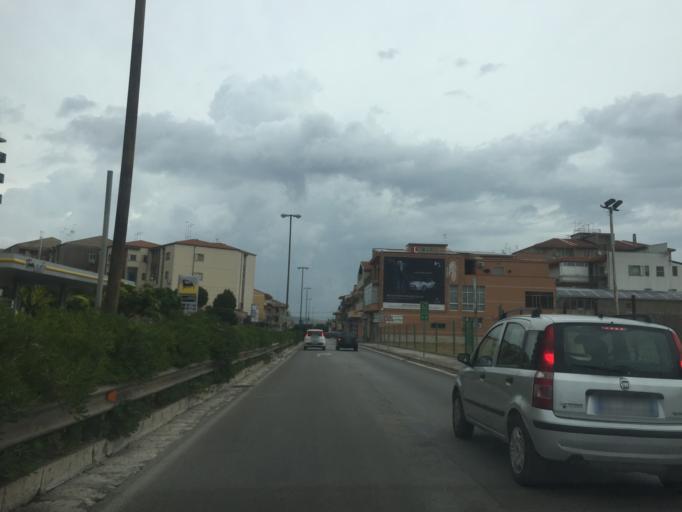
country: IT
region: Sicily
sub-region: Ragusa
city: Ragusa
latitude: 36.9095
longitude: 14.7230
